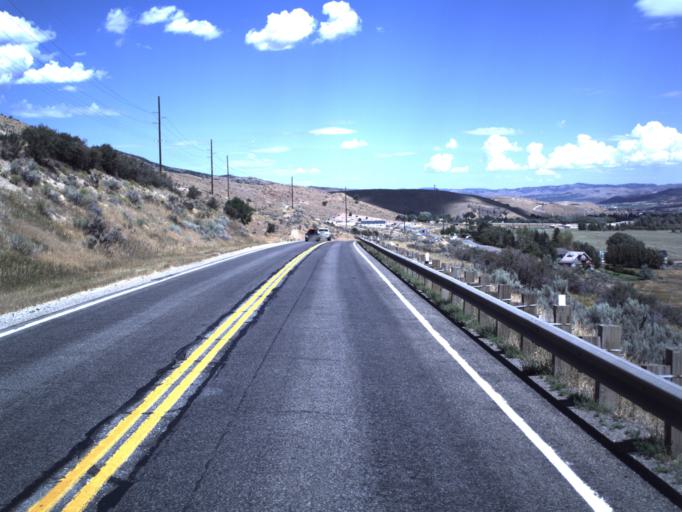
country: US
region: Utah
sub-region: Summit County
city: Coalville
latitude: 40.7925
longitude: -111.4098
